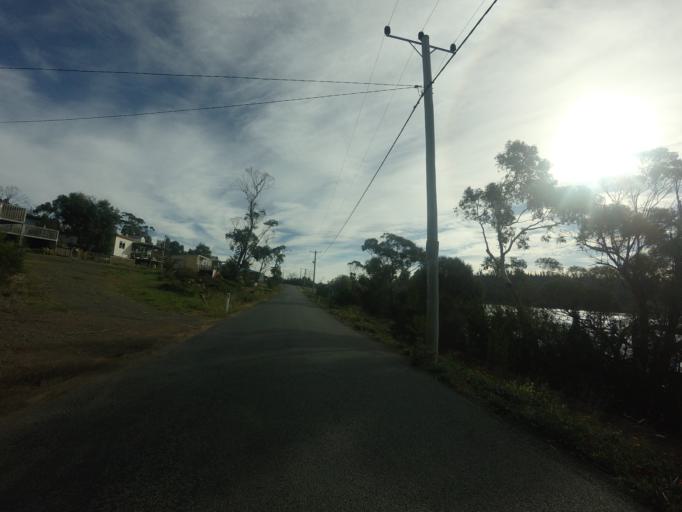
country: AU
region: Tasmania
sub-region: Sorell
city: Sorell
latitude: -42.9461
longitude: 147.8564
